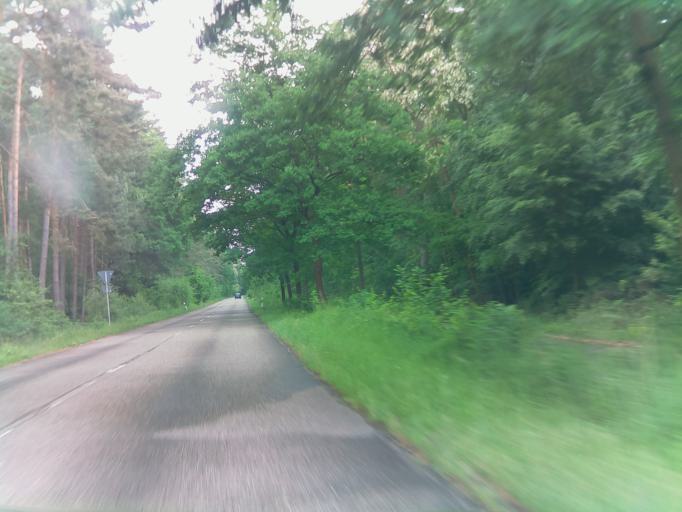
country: DE
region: Rheinland-Pfalz
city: Dudenhofen
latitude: 49.3470
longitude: 8.3814
